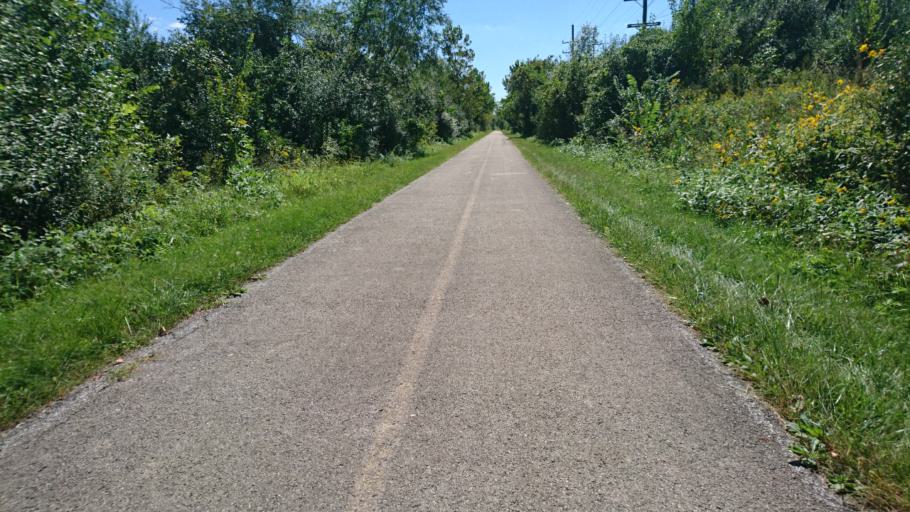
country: US
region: Illinois
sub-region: Cook County
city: Glenwood
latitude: 41.5280
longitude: -87.6227
